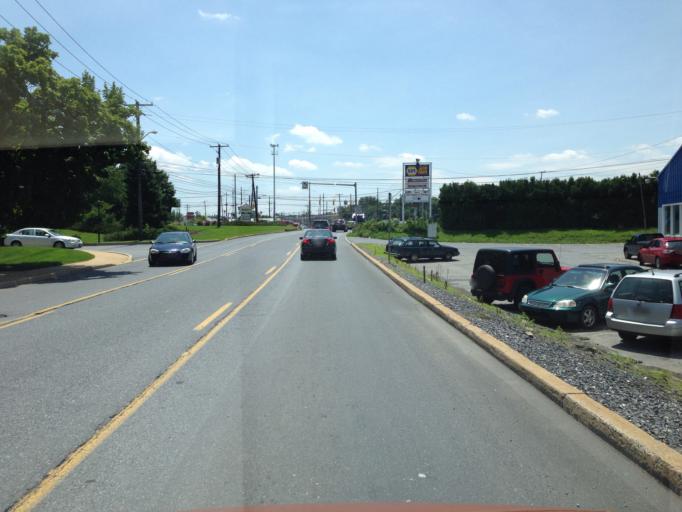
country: US
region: Pennsylvania
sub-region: Lancaster County
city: Lancaster
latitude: 40.0611
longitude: -76.3188
